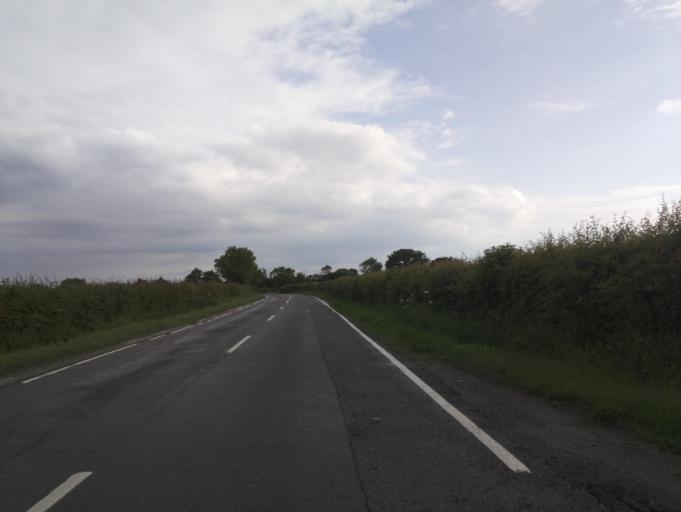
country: GB
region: England
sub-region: Lincolnshire
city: Great Gonerby
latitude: 53.0134
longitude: -0.6620
